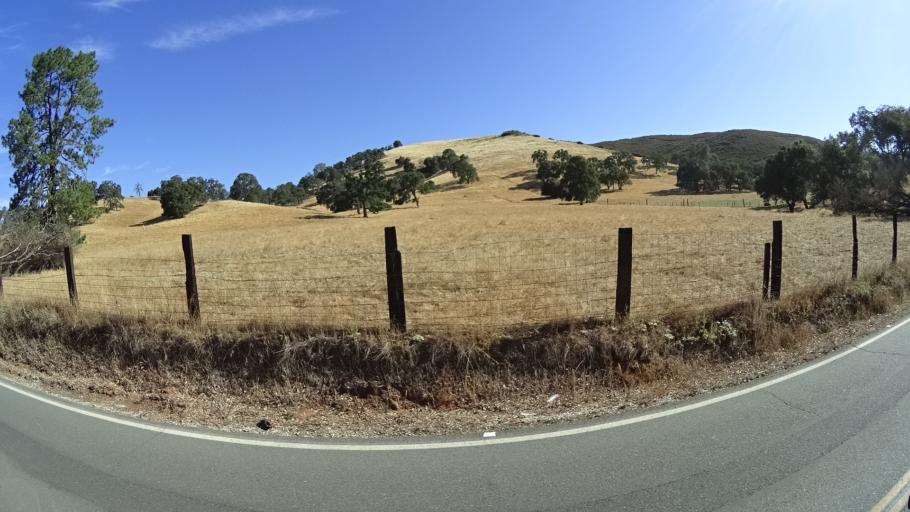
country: US
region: California
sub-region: Calaveras County
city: San Andreas
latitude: 38.1707
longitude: -120.6357
